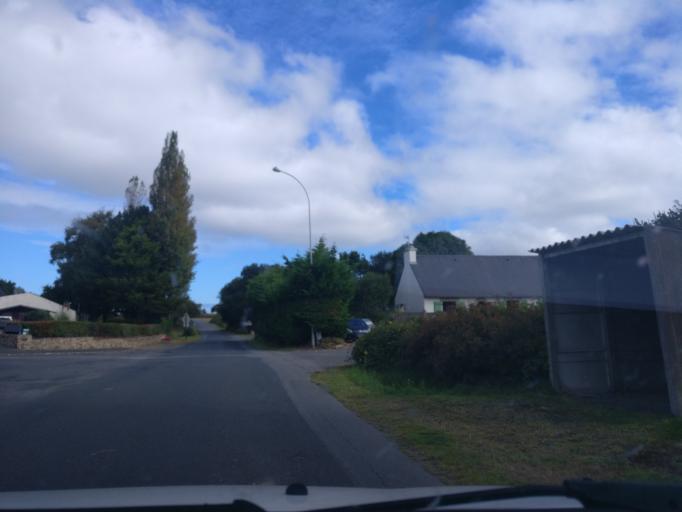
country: FR
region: Brittany
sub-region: Departement des Cotes-d'Armor
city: Rospez
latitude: 48.7622
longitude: -3.3678
